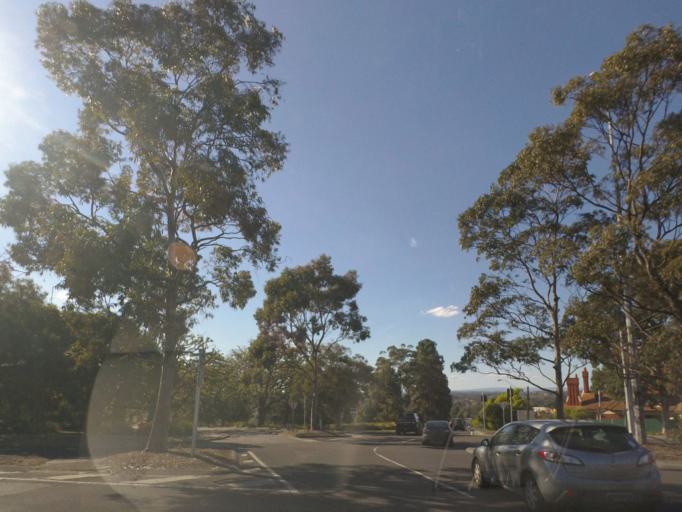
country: AU
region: Victoria
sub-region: Boroondara
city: Kew
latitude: -37.7992
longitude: 145.0302
